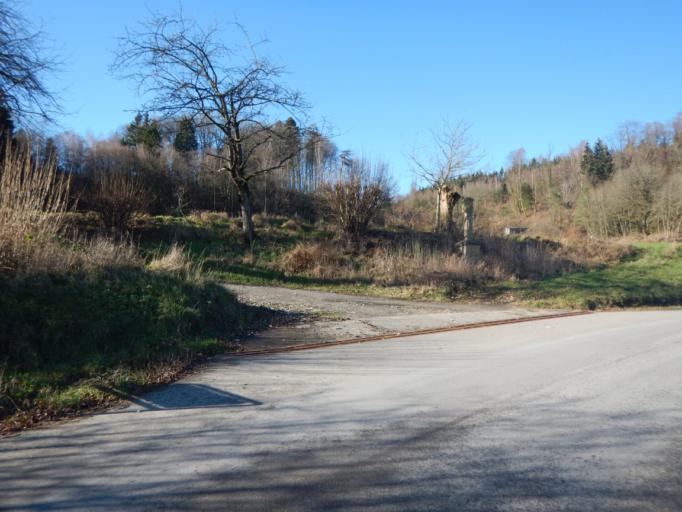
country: LU
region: Luxembourg
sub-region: Canton de Mersch
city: Lorentzweiler
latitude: 49.6934
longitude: 6.1661
